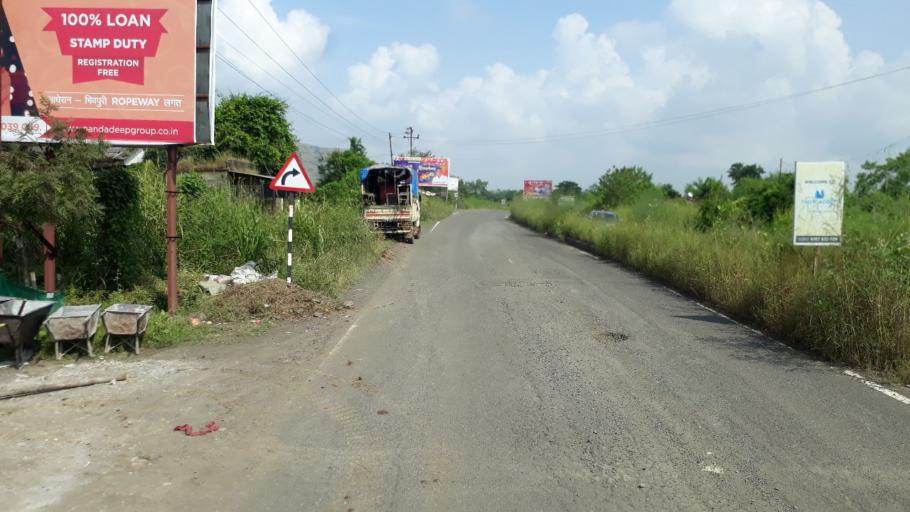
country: IN
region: Maharashtra
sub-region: Raigarh
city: Neral
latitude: 18.9879
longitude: 73.3276
